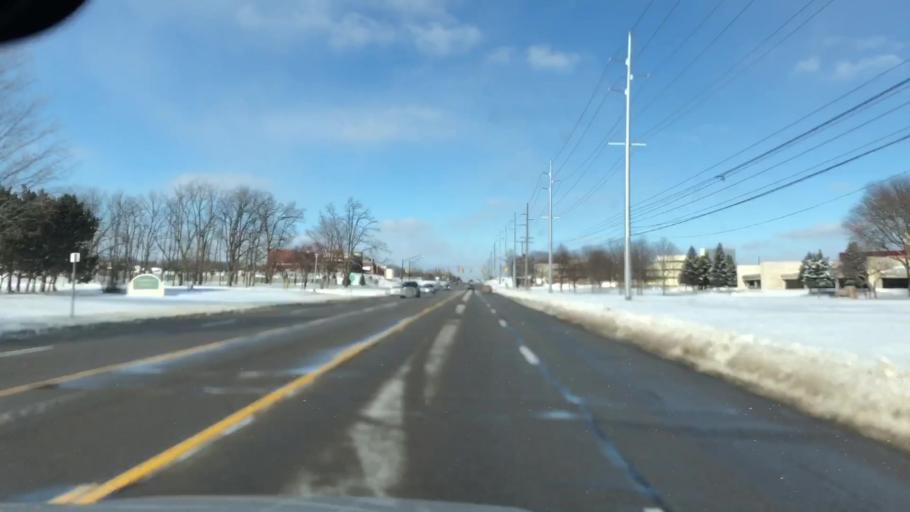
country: US
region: Michigan
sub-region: Wayne County
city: Northville
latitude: 42.4198
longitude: -83.4328
